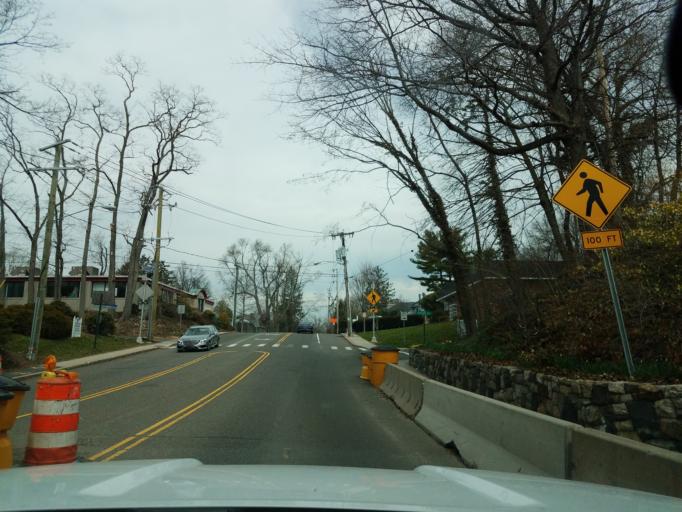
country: US
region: Connecticut
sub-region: Fairfield County
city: Riverside
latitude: 41.0332
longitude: -73.5686
